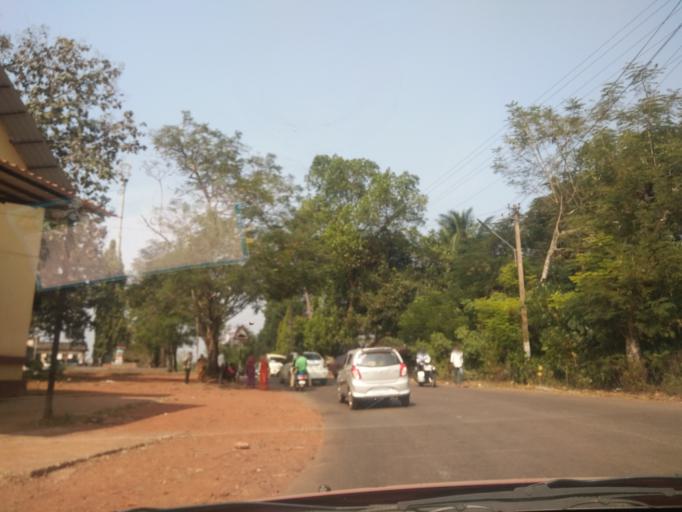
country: IN
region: Goa
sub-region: North Goa
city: Sanquelim
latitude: 15.5462
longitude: 74.0546
